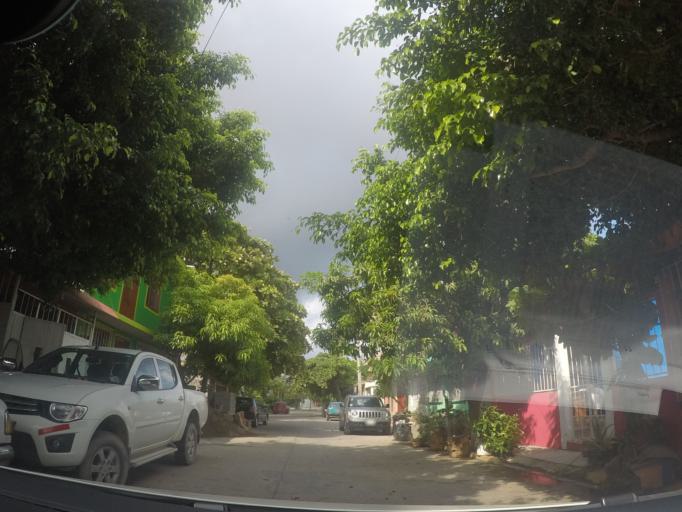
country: MX
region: Oaxaca
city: Juchitan de Zaragoza
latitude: 16.4349
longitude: -95.0333
